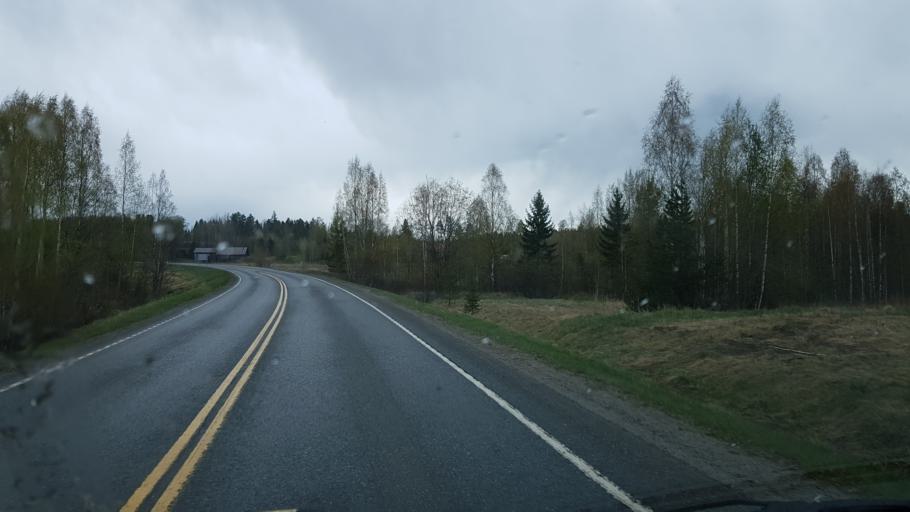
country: FI
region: Pirkanmaa
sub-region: Tampere
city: Pirkkala
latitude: 61.4239
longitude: 23.6346
